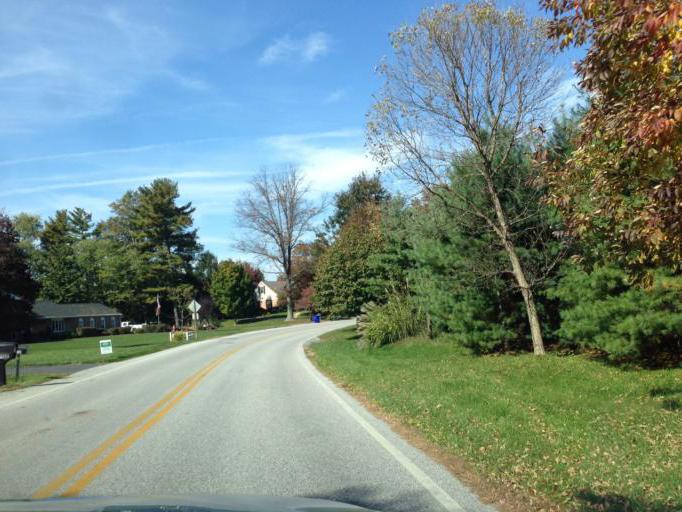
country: US
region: Maryland
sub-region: Howard County
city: Columbia
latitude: 39.2619
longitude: -76.8249
